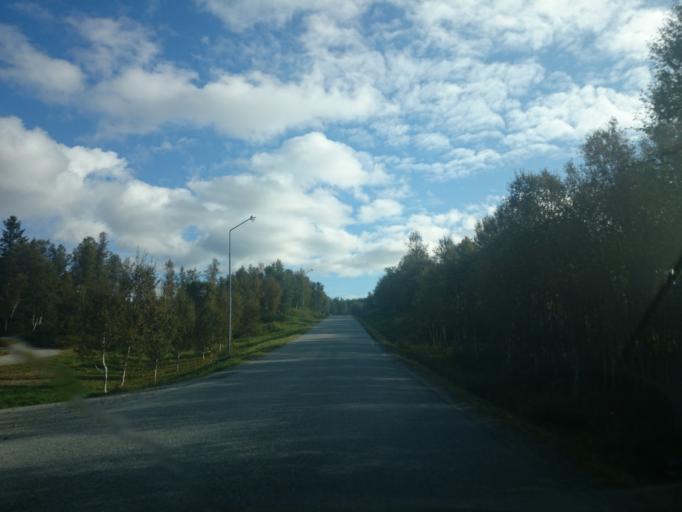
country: NO
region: Sor-Trondelag
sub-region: Tydal
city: Aas
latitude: 62.6421
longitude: 12.4212
